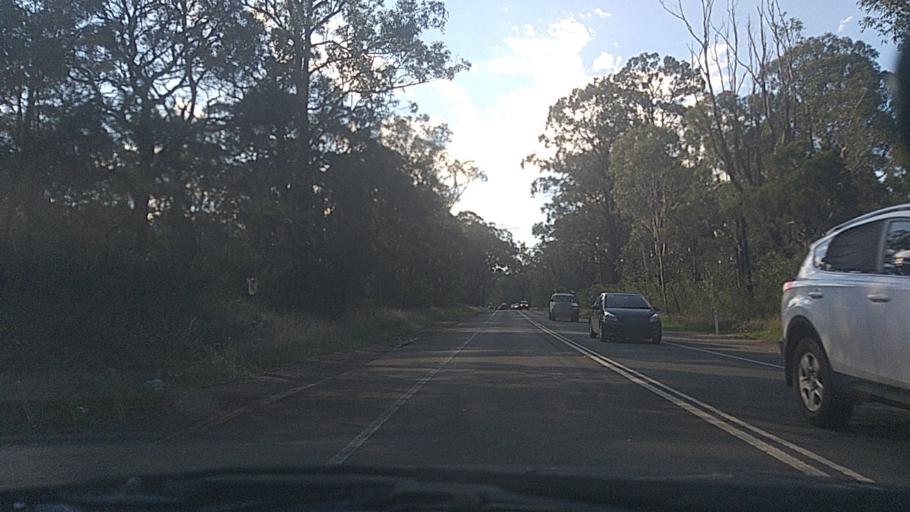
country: AU
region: New South Wales
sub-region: Hawkesbury
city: South Windsor
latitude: -33.6455
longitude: 150.7894
